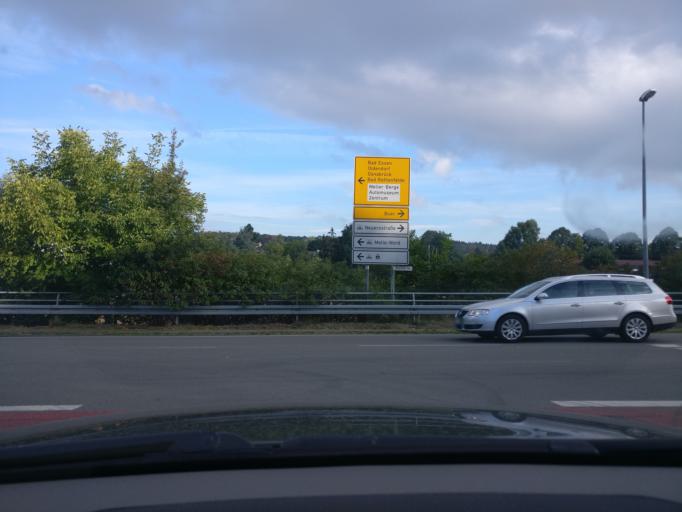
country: DE
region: Lower Saxony
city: Melle
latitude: 52.2076
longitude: 8.3519
